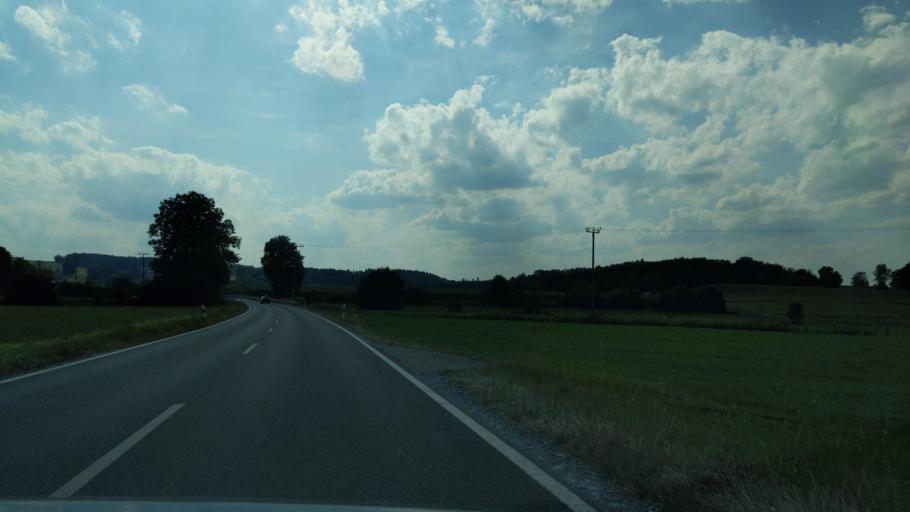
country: DE
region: Bavaria
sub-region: Upper Bavaria
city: Bruck
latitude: 48.0240
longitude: 11.9123
